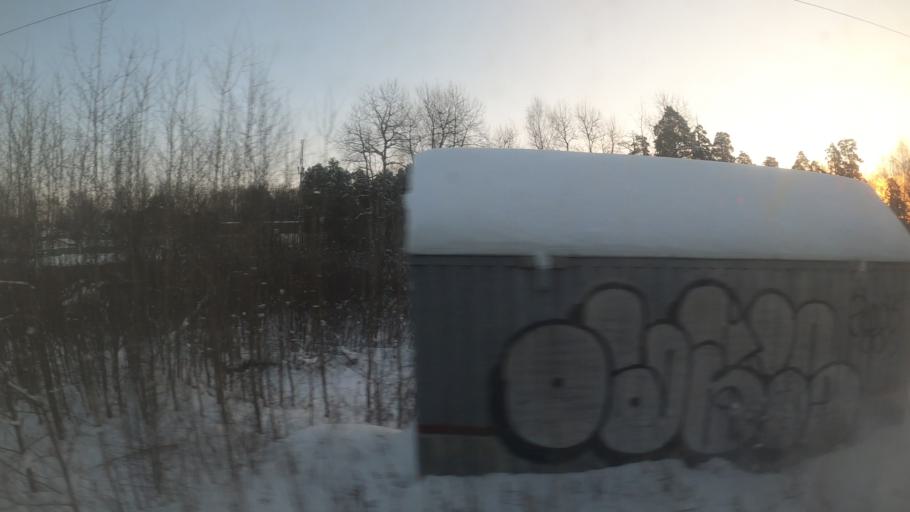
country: RU
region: Moskovskaya
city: Dedenevo
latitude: 56.2358
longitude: 37.5139
